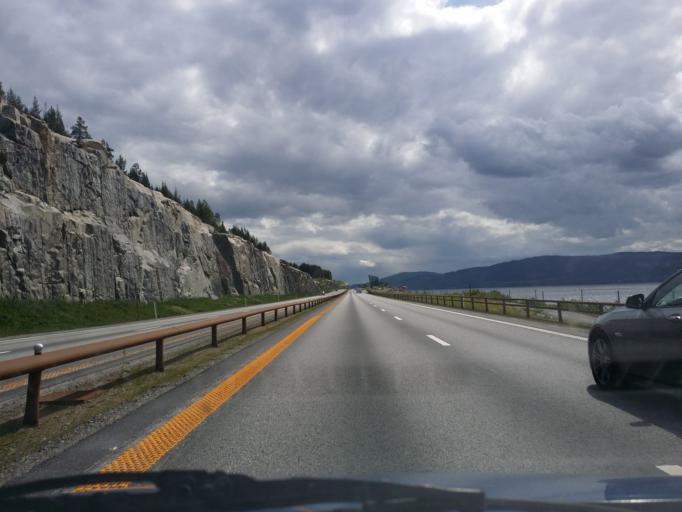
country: NO
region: Hedmark
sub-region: Stange
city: Stange
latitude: 60.5439
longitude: 11.2473
